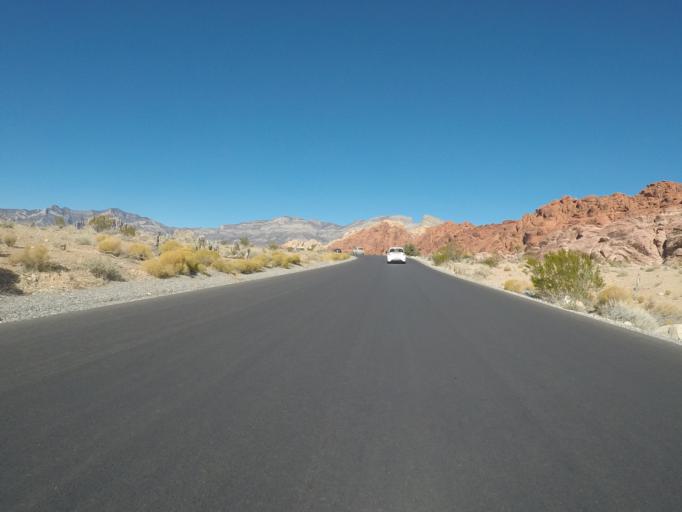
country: US
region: Nevada
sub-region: Clark County
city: Summerlin South
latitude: 36.1440
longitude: -115.4291
